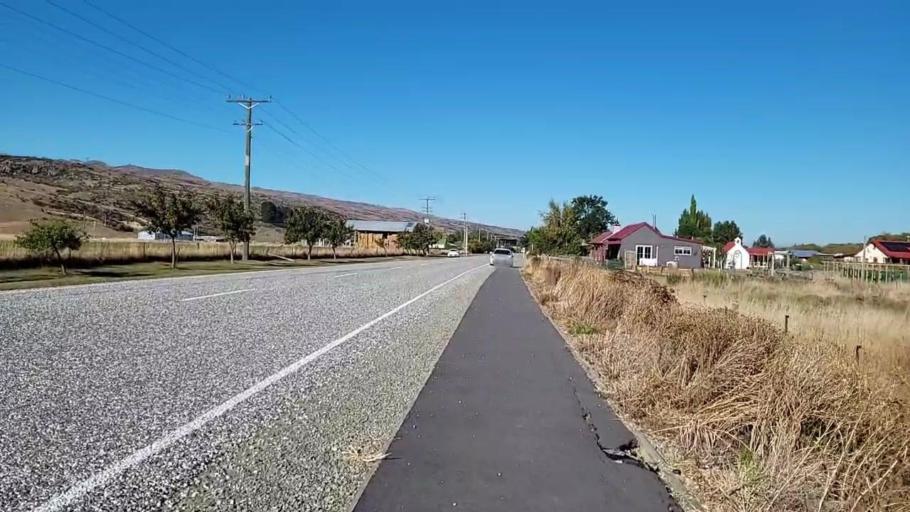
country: NZ
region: Otago
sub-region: Queenstown-Lakes District
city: Wanaka
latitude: -45.0040
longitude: 169.9160
